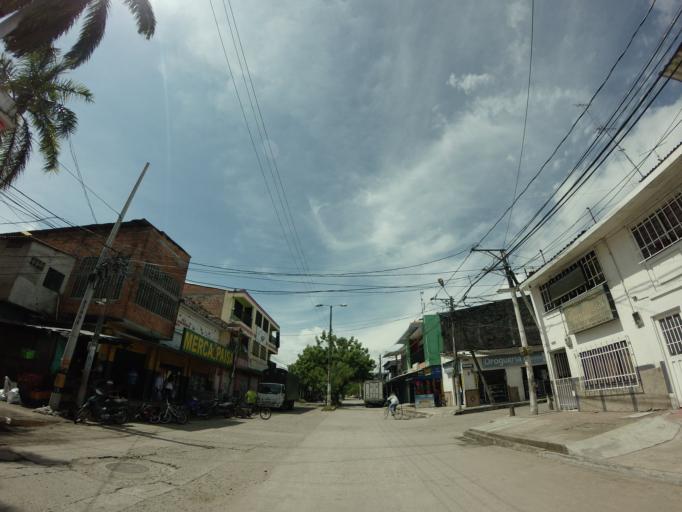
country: CO
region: Cundinamarca
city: Puerto Salgar
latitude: 5.4782
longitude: -74.6748
